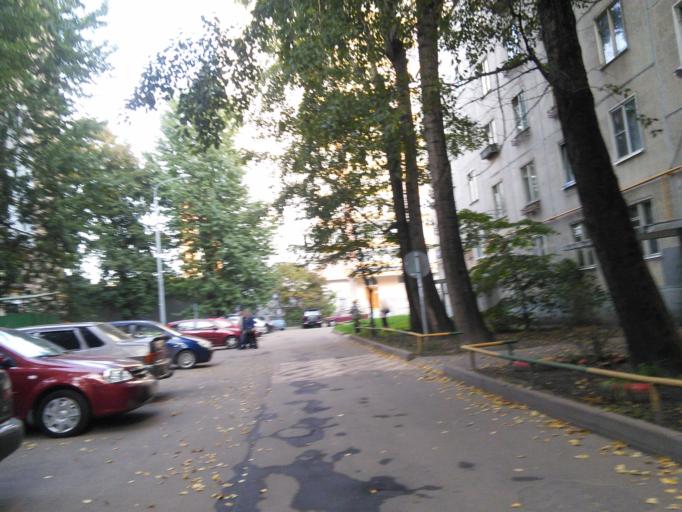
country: RU
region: Moscow
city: Kozeyevo
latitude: 55.8733
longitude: 37.6353
